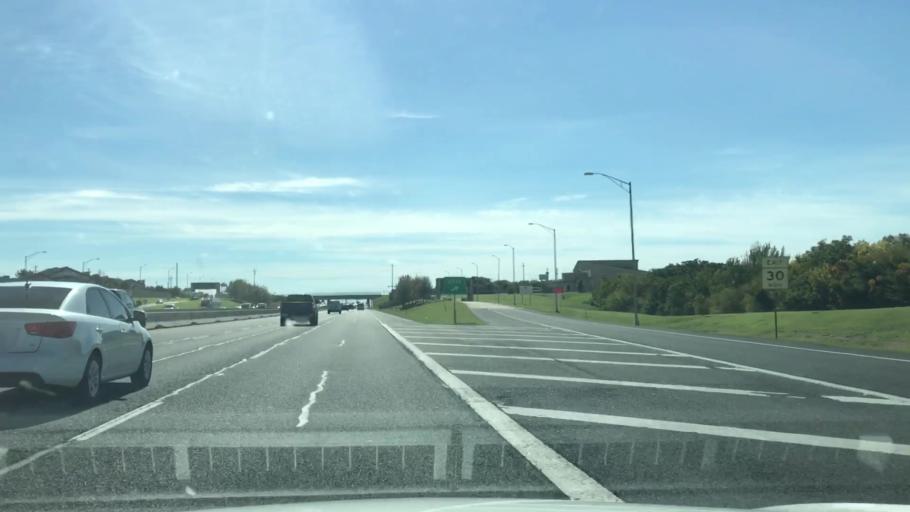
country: US
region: Texas
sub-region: Dallas County
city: Addison
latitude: 33.0030
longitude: -96.8541
